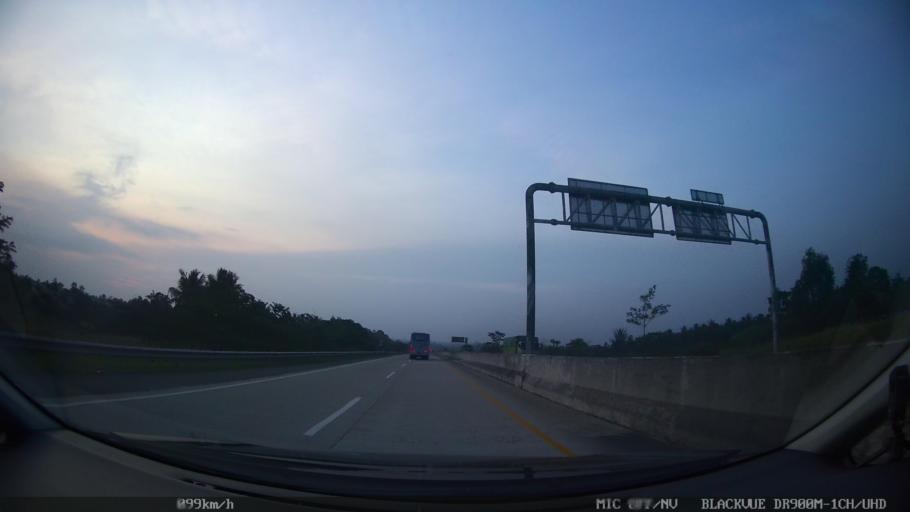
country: ID
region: Lampung
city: Kalianda
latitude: -5.6867
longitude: 105.6165
